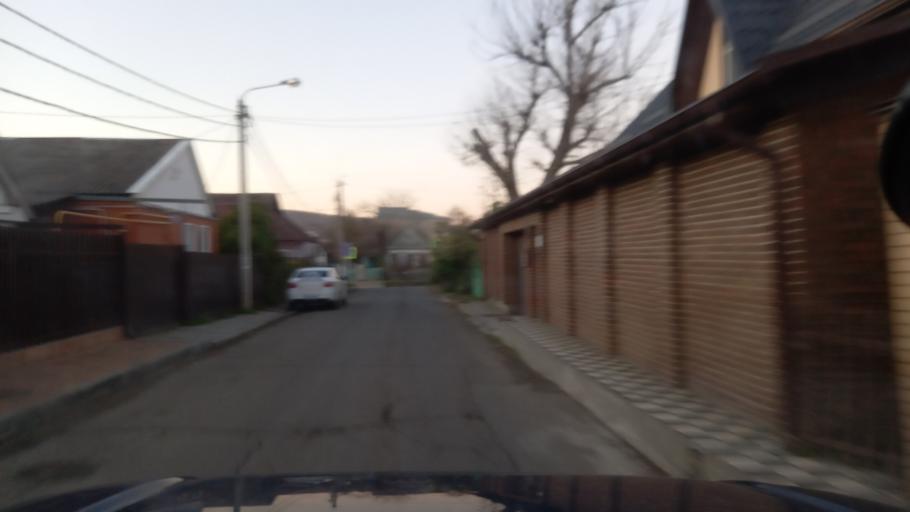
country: RU
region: Krasnodarskiy
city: Goryachiy Klyuch
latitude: 44.6273
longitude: 39.1025
